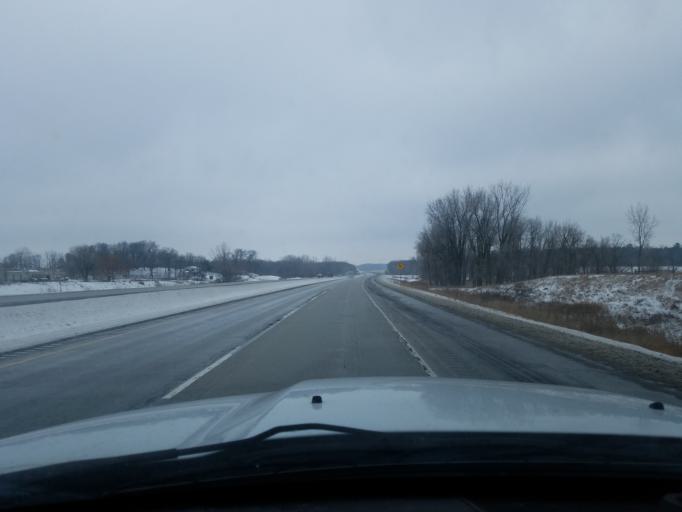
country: US
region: Indiana
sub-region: Fulton County
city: Rochester
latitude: 41.0866
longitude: -86.2409
